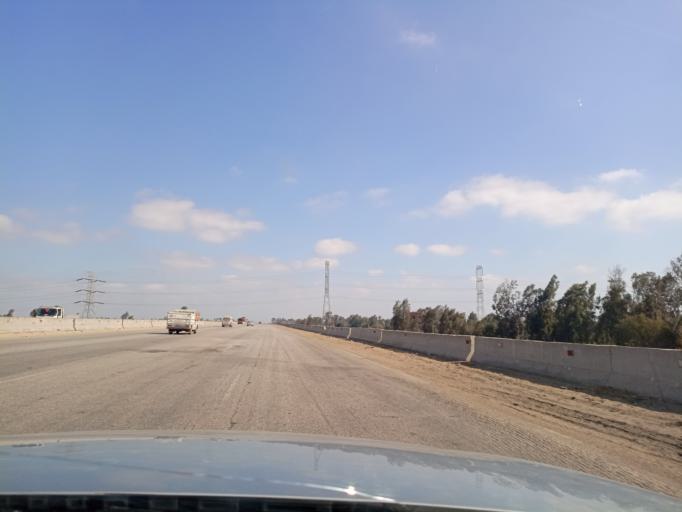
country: EG
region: Muhafazat al Qalyubiyah
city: Banha
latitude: 30.4385
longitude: 31.1099
